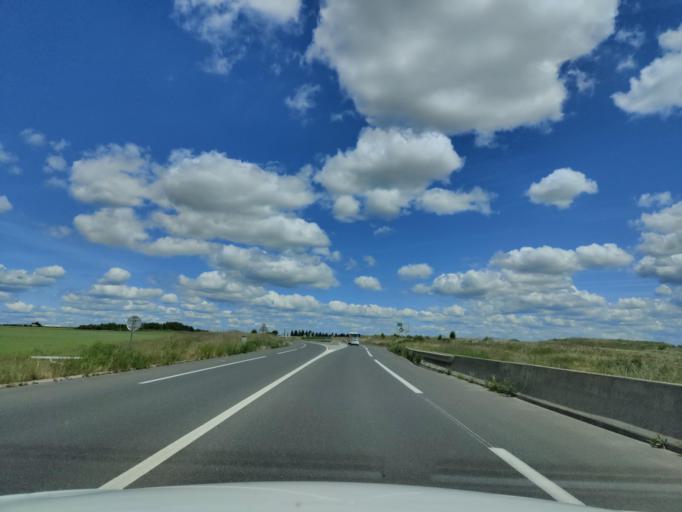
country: FR
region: Centre
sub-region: Departement du Cher
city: Saint-Germain-du-Puy
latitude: 47.1037
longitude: 2.4440
